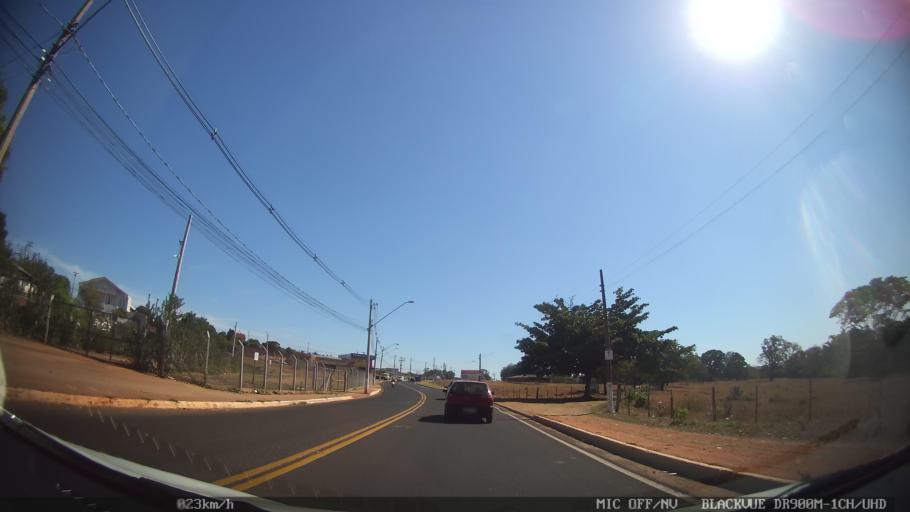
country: BR
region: Sao Paulo
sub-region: Sao Jose Do Rio Preto
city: Sao Jose do Rio Preto
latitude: -20.7697
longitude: -49.4180
